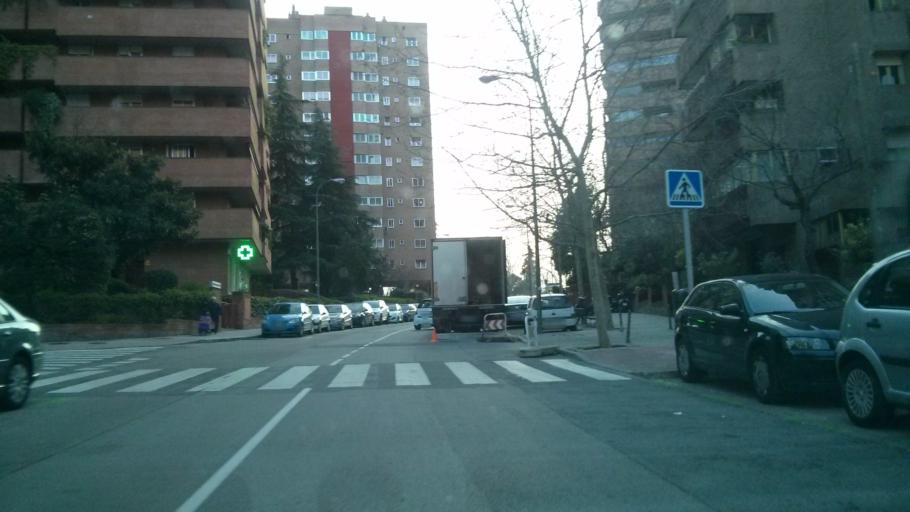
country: ES
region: Madrid
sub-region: Provincia de Madrid
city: Tetuan de las Victorias
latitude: 40.4765
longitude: -3.6993
